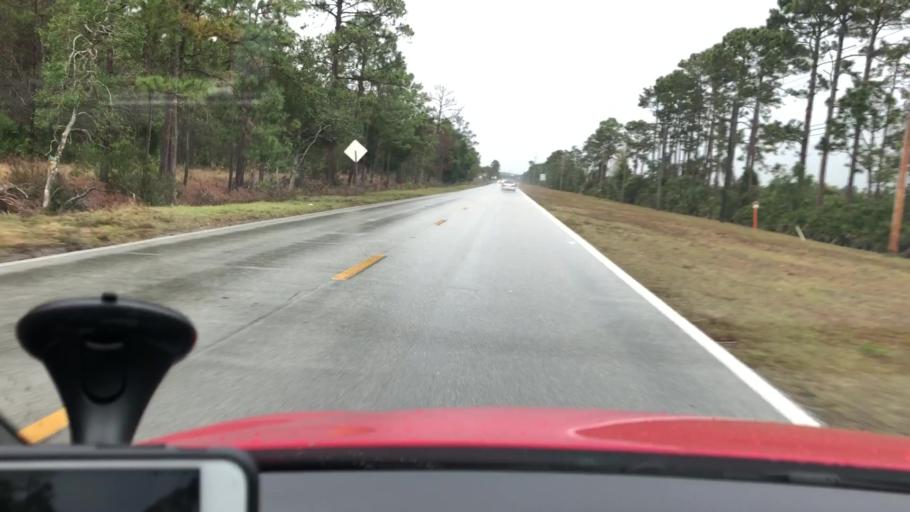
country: US
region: Florida
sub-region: Volusia County
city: Ormond Beach
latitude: 29.2427
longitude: -81.1015
